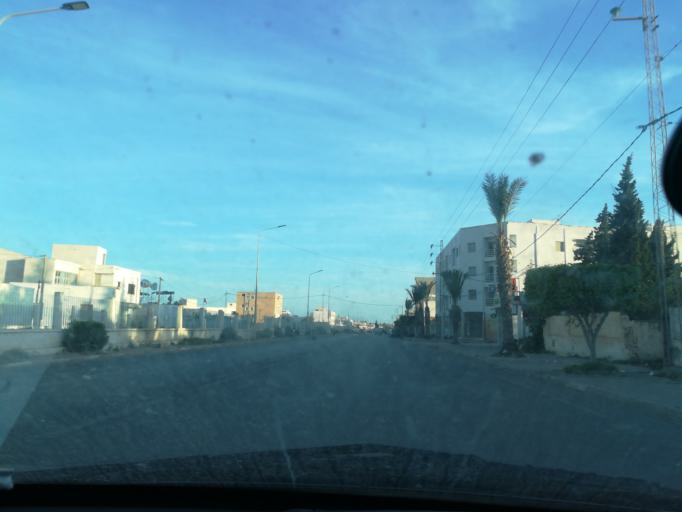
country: TN
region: Safaqis
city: Al Qarmadah
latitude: 34.8069
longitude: 10.7615
